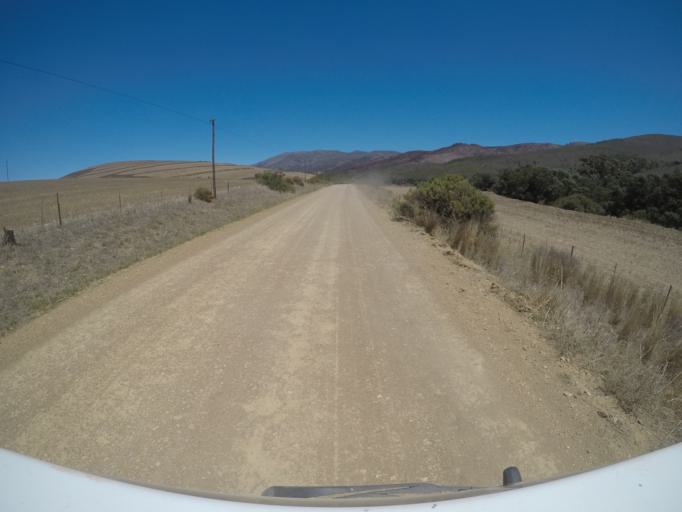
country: ZA
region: Western Cape
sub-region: Overberg District Municipality
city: Caledon
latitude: -34.1504
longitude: 19.2395
